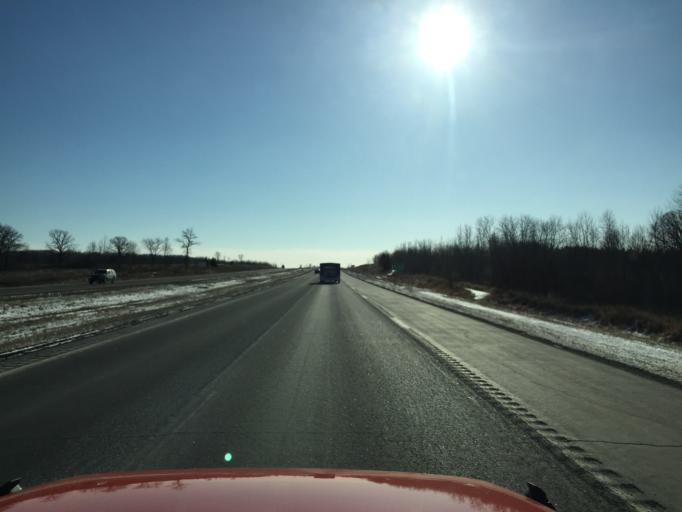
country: US
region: Minnesota
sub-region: Mille Lacs County
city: Milaca
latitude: 45.7762
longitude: -93.6477
